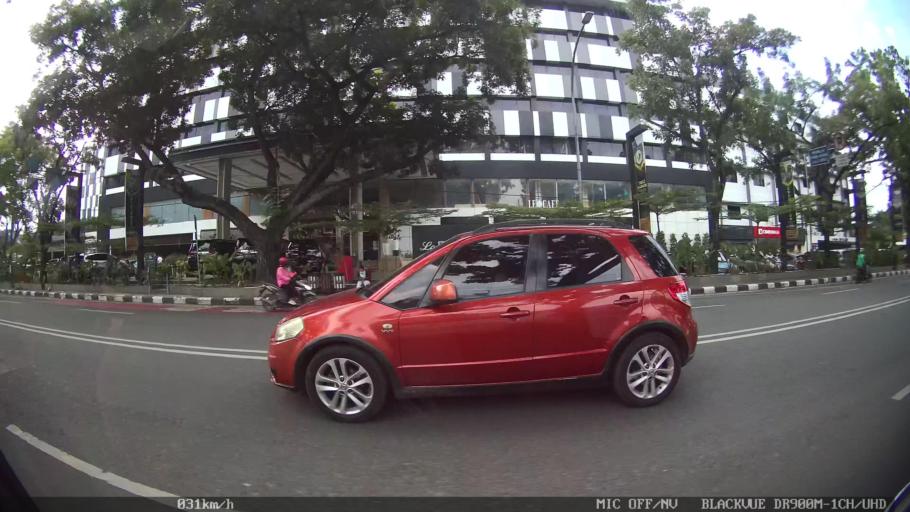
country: ID
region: North Sumatra
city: Medan
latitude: 3.5769
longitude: 98.6762
